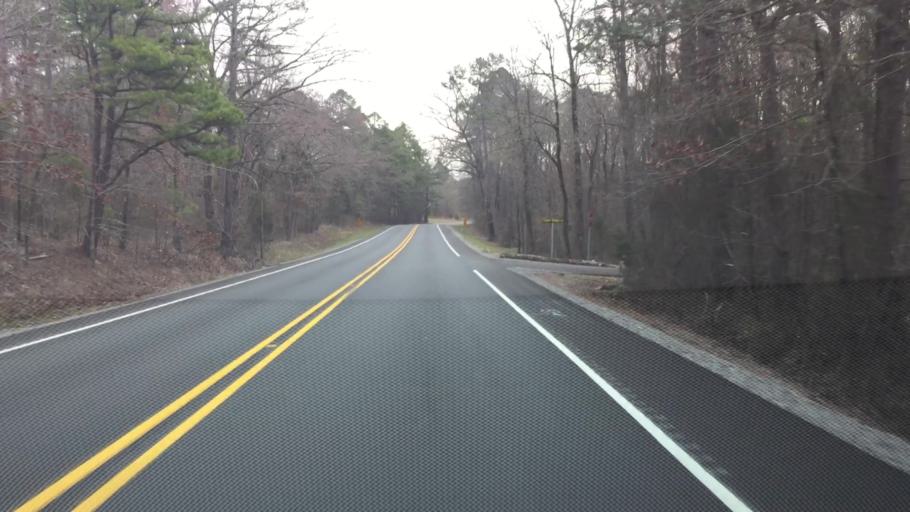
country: US
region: Arkansas
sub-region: Saline County
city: Haskell
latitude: 34.6118
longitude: -92.8005
